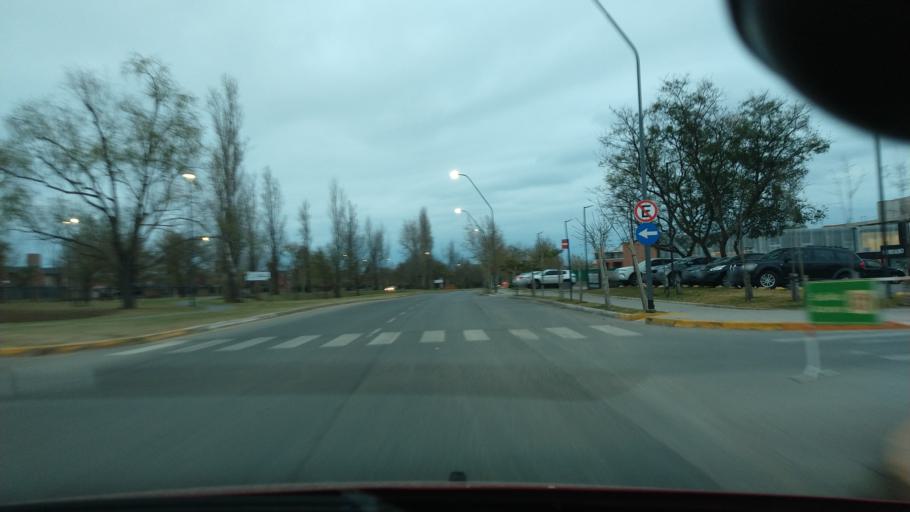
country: AR
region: Cordoba
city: La Calera
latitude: -31.3732
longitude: -64.2774
